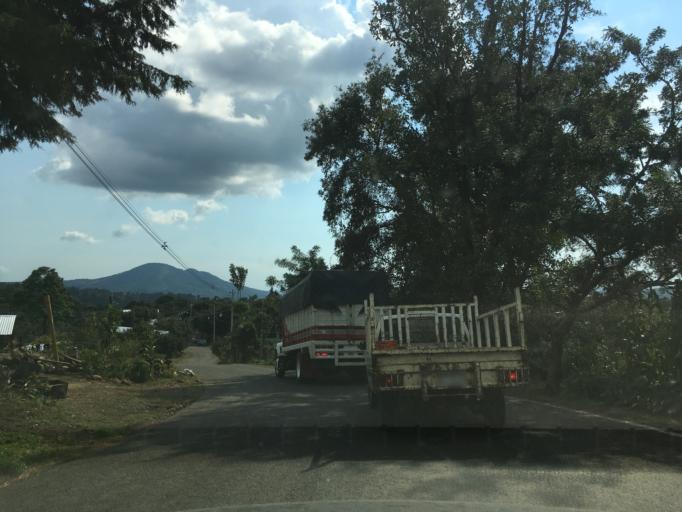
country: MX
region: Michoacan
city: Tingambato
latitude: 19.4533
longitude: -101.8668
